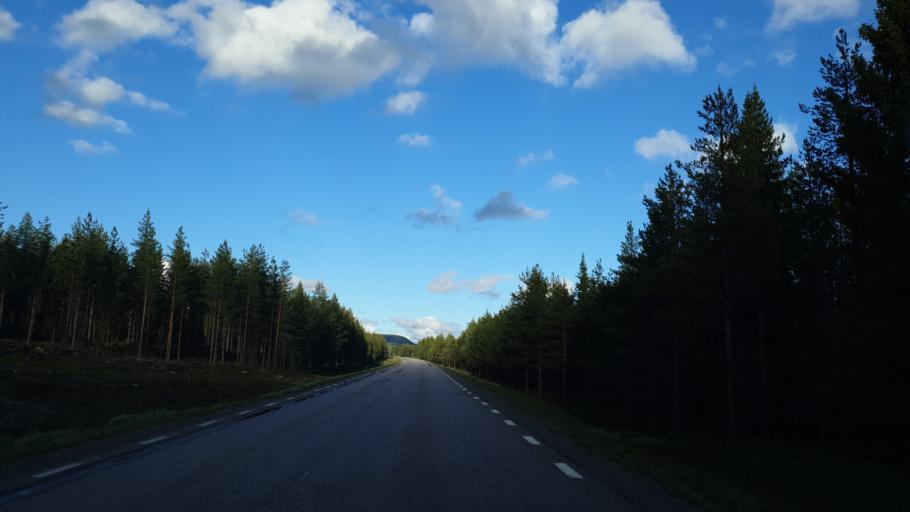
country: SE
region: Norrbotten
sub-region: Arvidsjaurs Kommun
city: Arvidsjaur
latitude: 65.7325
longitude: 18.6410
